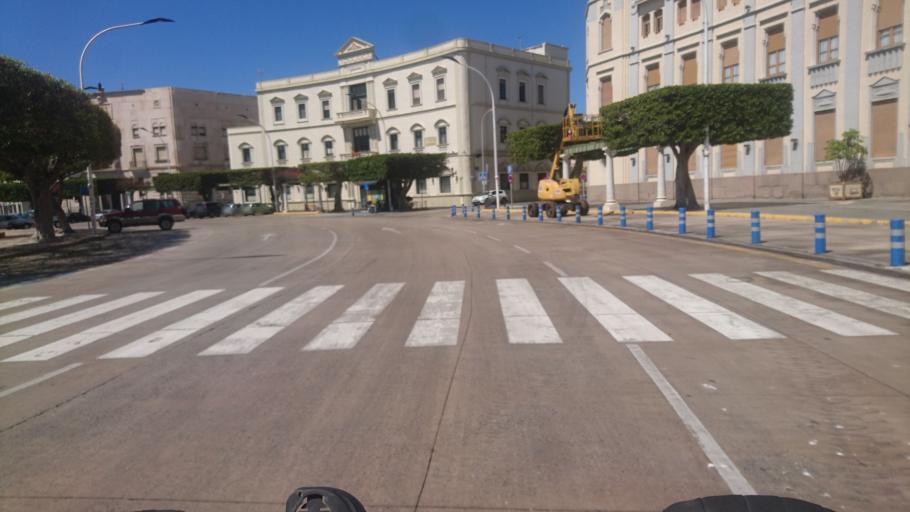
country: ES
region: Melilla
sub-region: Melilla
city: Melilla
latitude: 35.2921
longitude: -2.9373
